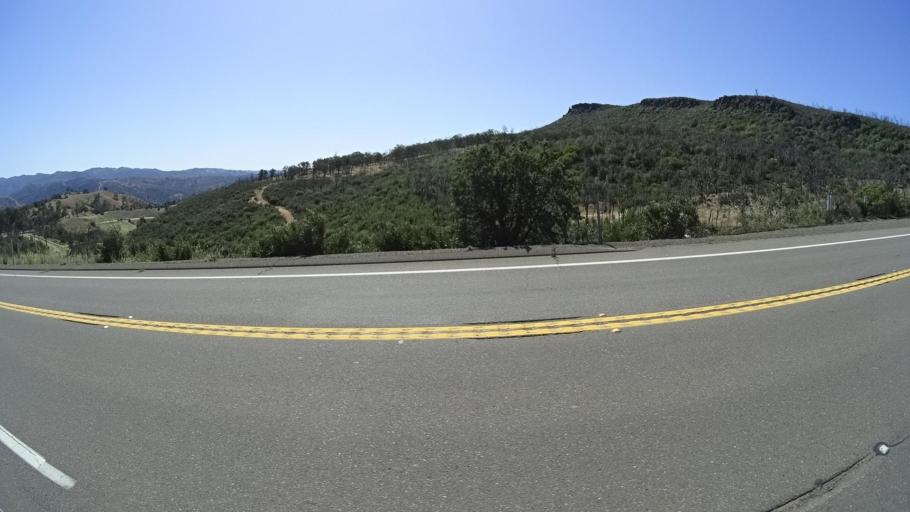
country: US
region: California
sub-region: Lake County
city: Clearlake
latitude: 39.0166
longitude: -122.6002
